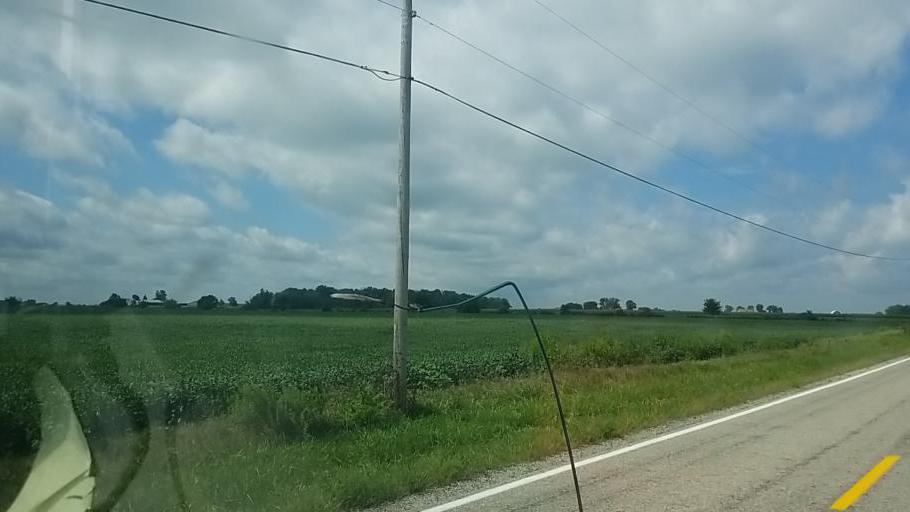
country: US
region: Ohio
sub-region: Madison County
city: Bethel
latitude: 39.7315
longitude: -83.4078
